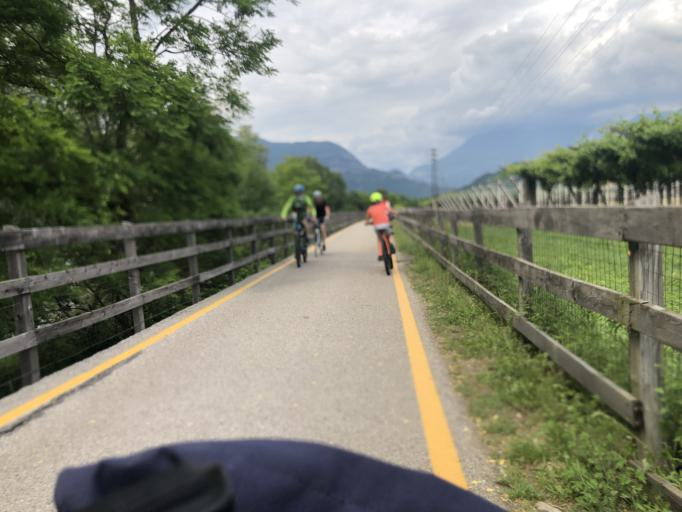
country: IT
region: Trentino-Alto Adige
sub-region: Provincia di Trento
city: Isera
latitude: 45.8942
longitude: 11.0202
